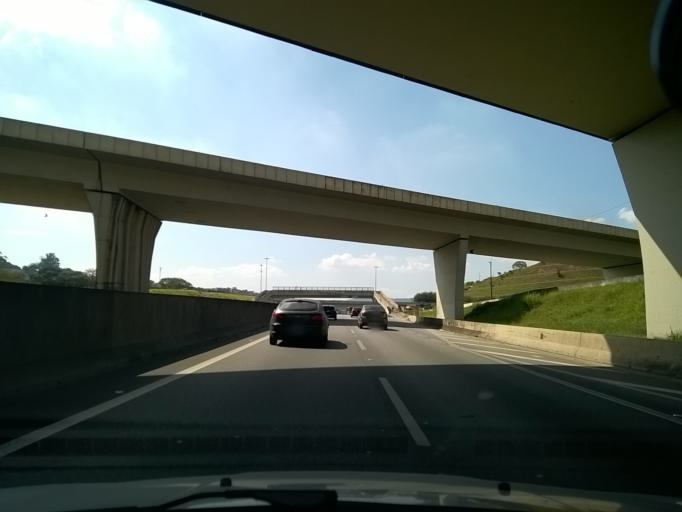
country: BR
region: Sao Paulo
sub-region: Osasco
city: Osasco
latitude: -23.4512
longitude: -46.7869
